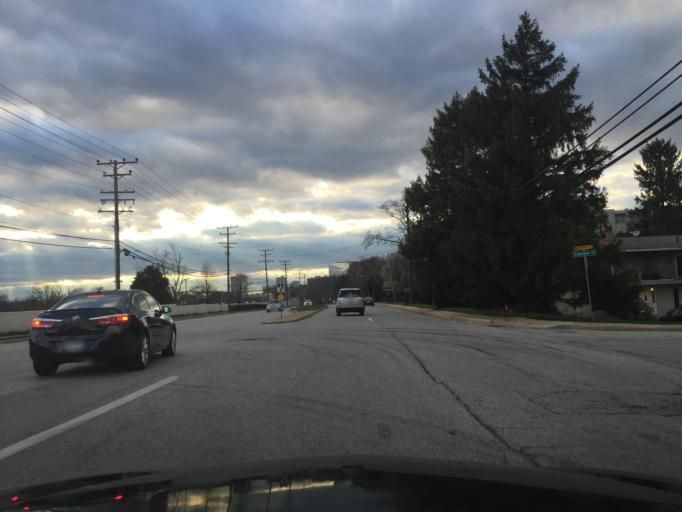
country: US
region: Maryland
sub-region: Baltimore County
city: Towson
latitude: 39.3972
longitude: -76.5802
